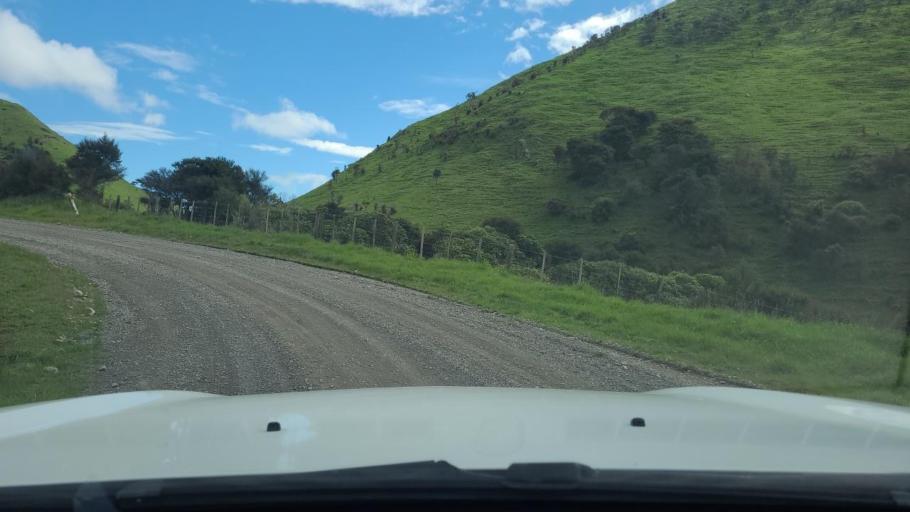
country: NZ
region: Wellington
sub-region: South Wairarapa District
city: Waipawa
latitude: -41.3255
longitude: 175.3955
